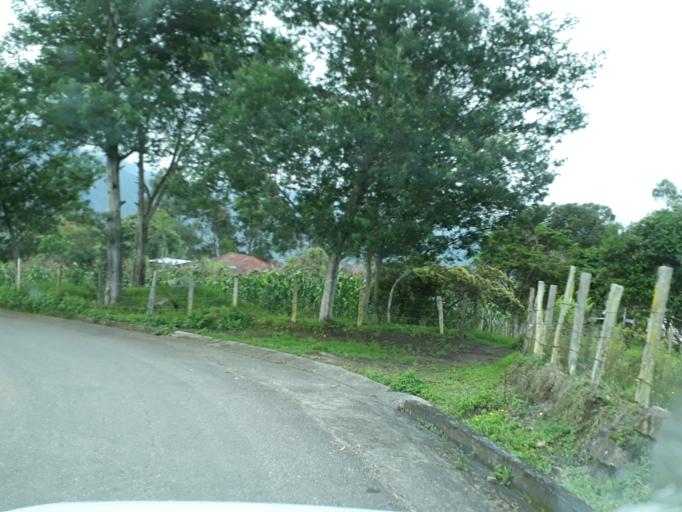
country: CO
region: Cundinamarca
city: Junin
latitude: 4.8016
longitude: -73.6772
